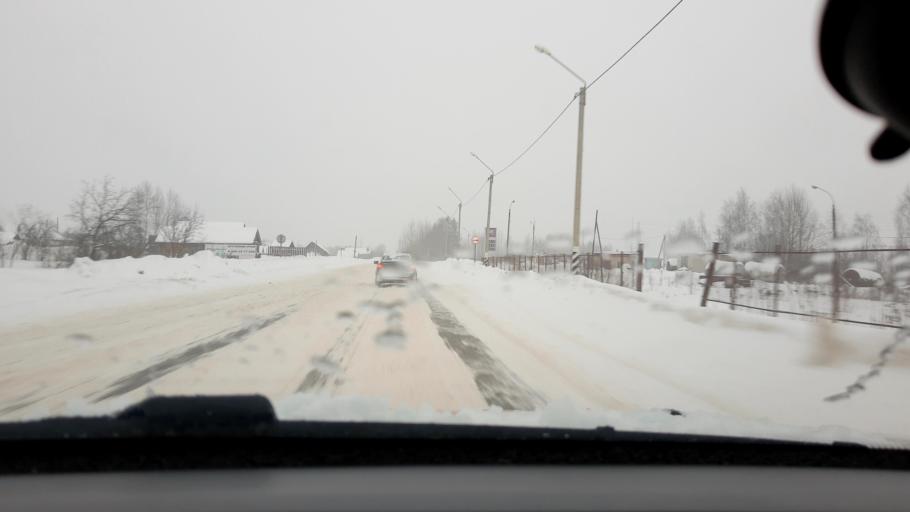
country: RU
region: Nizjnij Novgorod
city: Purekh
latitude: 56.6662
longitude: 43.1041
